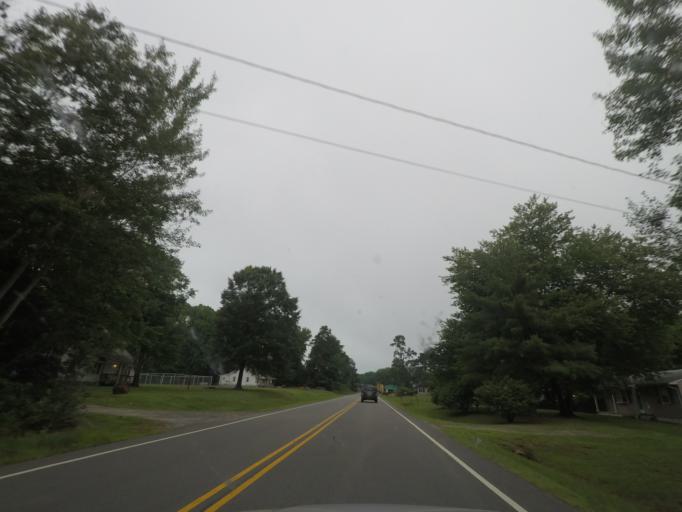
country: US
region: Virginia
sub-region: Prince Edward County
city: Hampden Sydney
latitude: 37.2430
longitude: -78.4435
